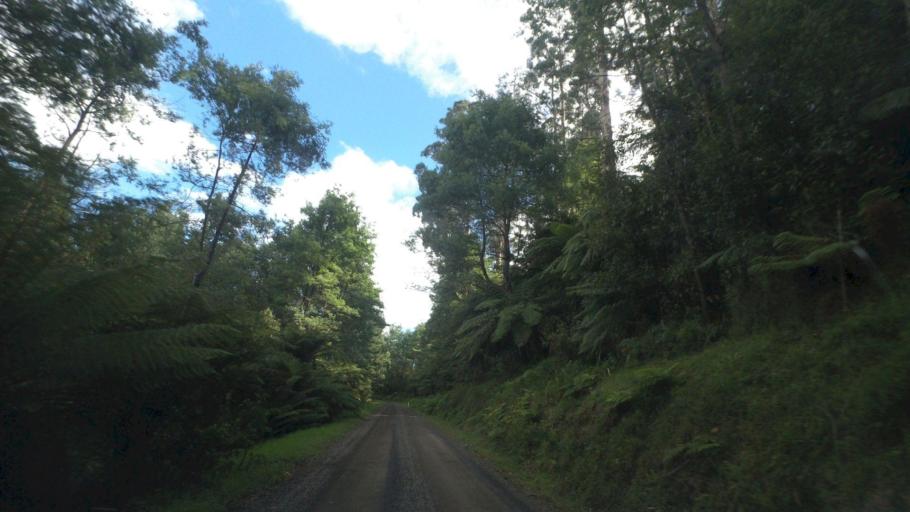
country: AU
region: Victoria
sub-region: Cardinia
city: Bunyip
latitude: -37.9498
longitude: 145.8182
